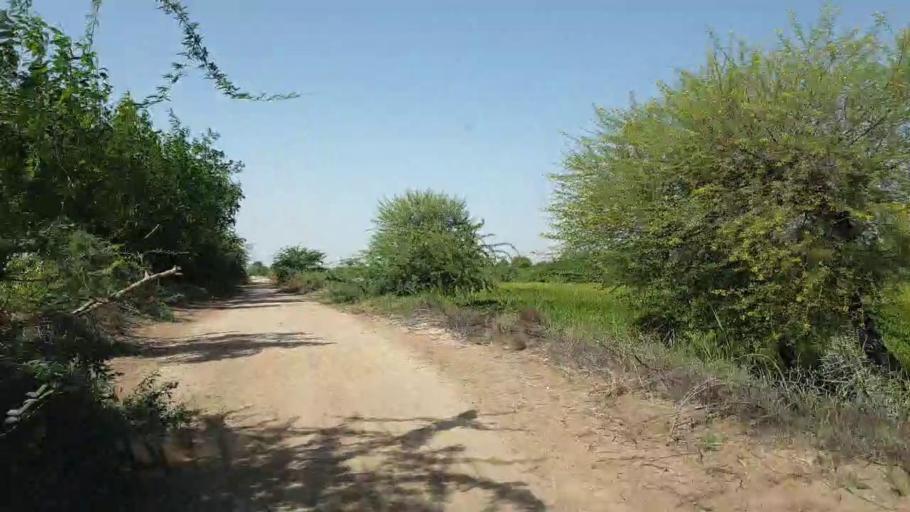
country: PK
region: Sindh
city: Tando Bago
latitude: 24.7415
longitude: 69.0432
